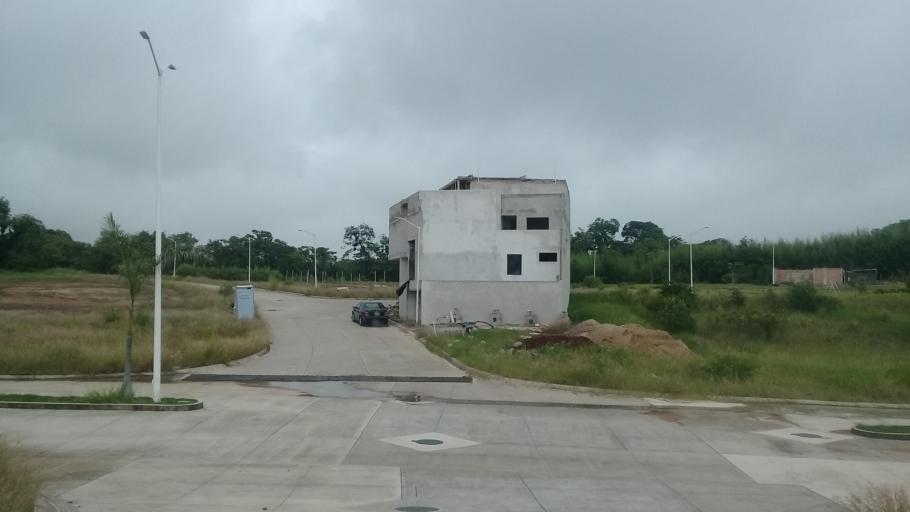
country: MX
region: Veracruz
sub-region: Emiliano Zapata
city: Jacarandas
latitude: 19.5058
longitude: -96.8462
